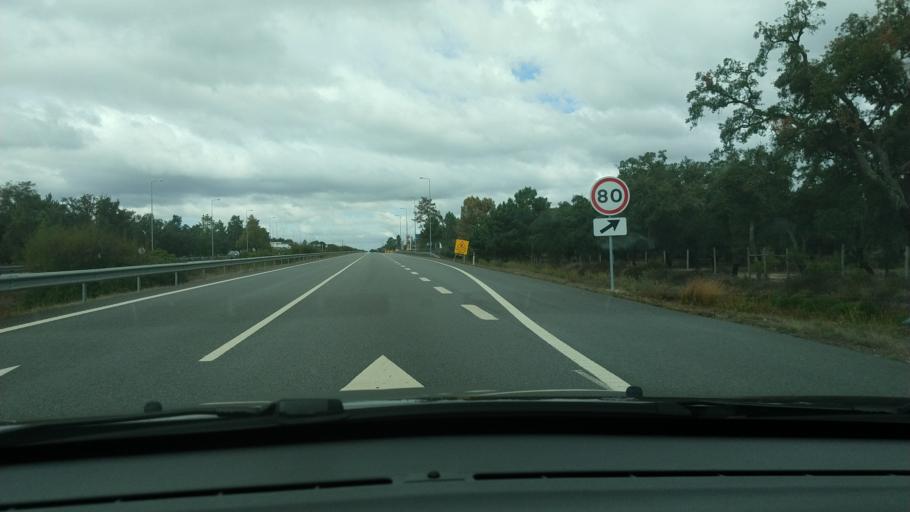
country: PT
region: Setubal
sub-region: Alcacer do Sal
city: Alcacer do Sal
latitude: 38.5119
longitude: -8.5826
